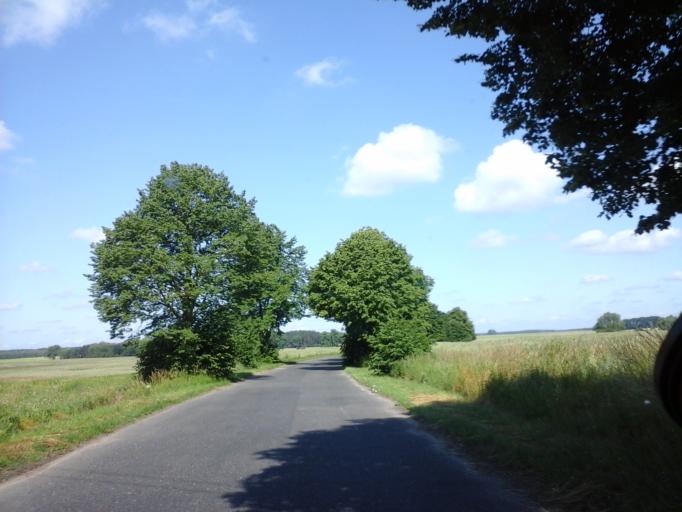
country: PL
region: West Pomeranian Voivodeship
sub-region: Powiat choszczenski
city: Recz
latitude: 53.1912
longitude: 15.5801
